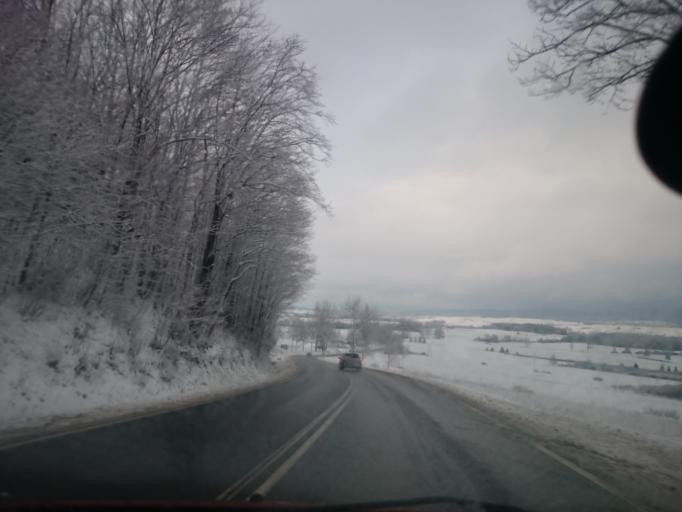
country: PL
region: Lower Silesian Voivodeship
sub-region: Powiat klodzki
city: Bystrzyca Klodzka
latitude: 50.3509
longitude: 16.6644
